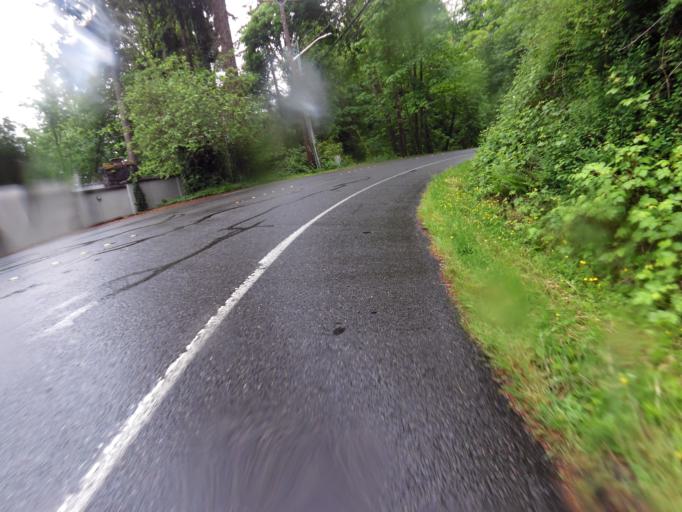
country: US
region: Washington
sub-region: King County
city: Mercer Island
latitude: 47.5546
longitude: -122.2126
